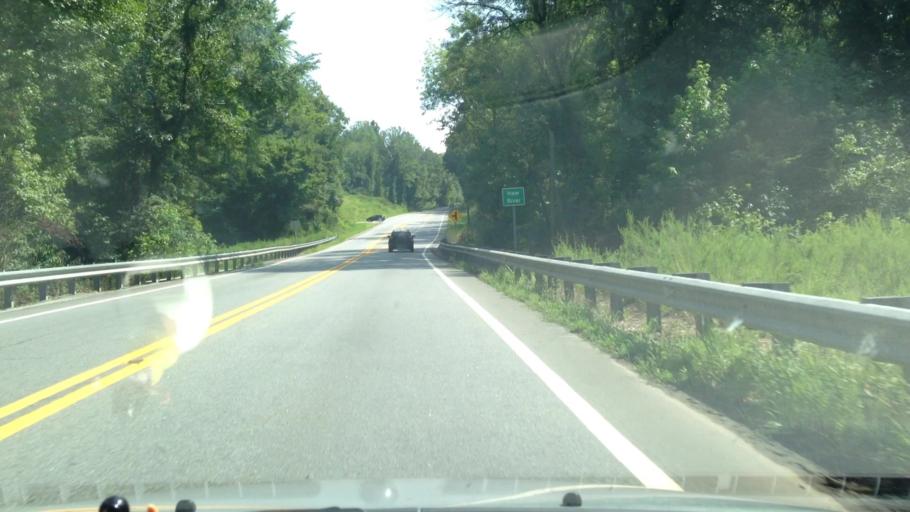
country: US
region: North Carolina
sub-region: Guilford County
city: Oak Ridge
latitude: 36.1984
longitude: -79.9854
